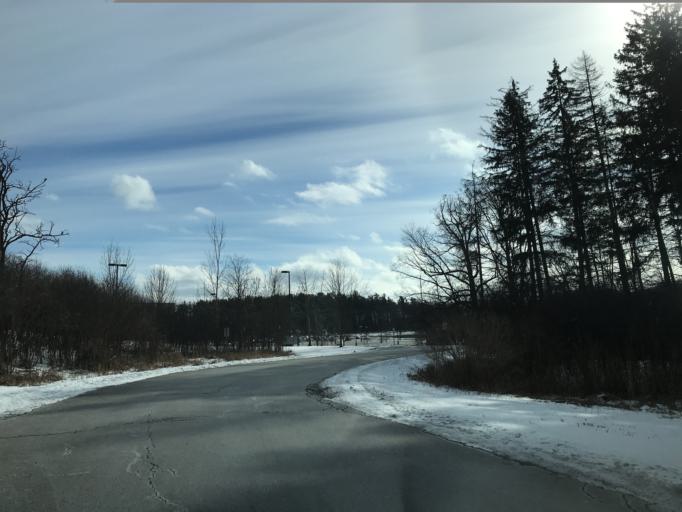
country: US
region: Michigan
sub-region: Washtenaw County
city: Ypsilanti
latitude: 42.2648
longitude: -83.6700
